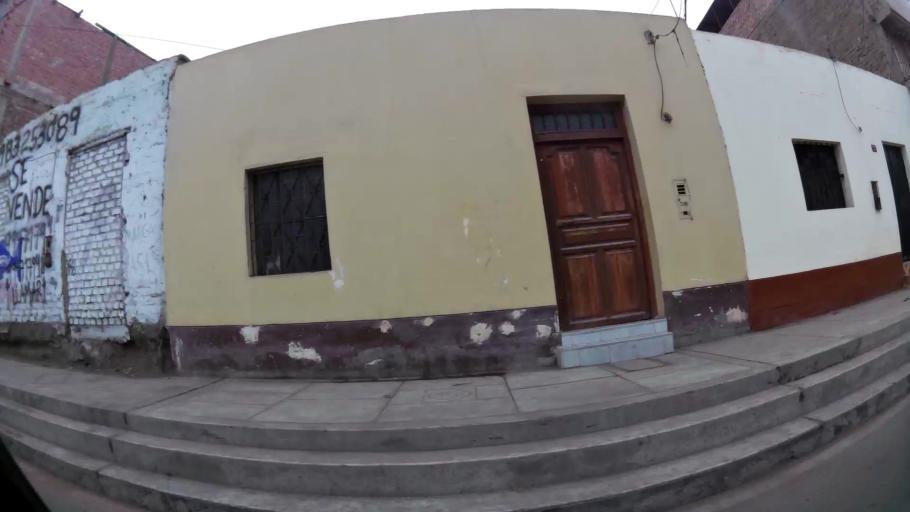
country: PE
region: Lima
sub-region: Barranca
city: Barranca
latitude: -10.7465
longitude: -77.7576
